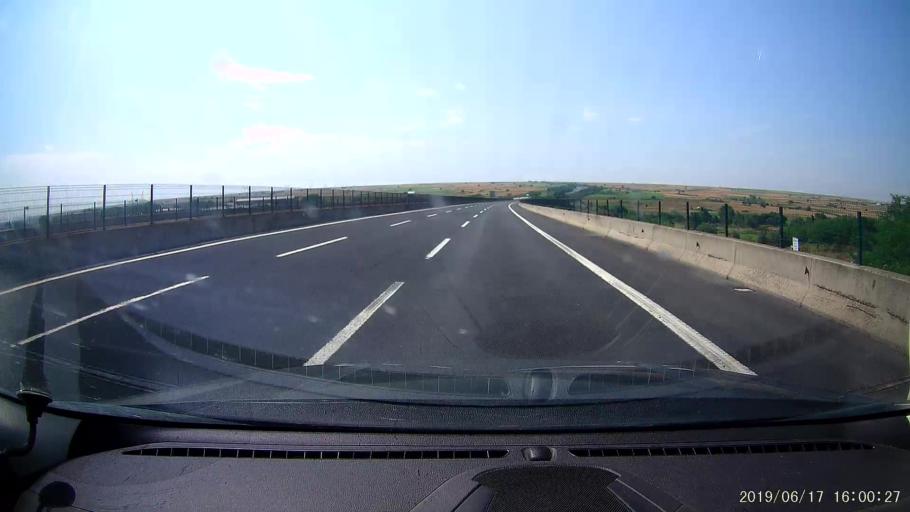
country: TR
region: Tekirdag
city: Velimese
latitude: 41.2326
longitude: 27.8694
